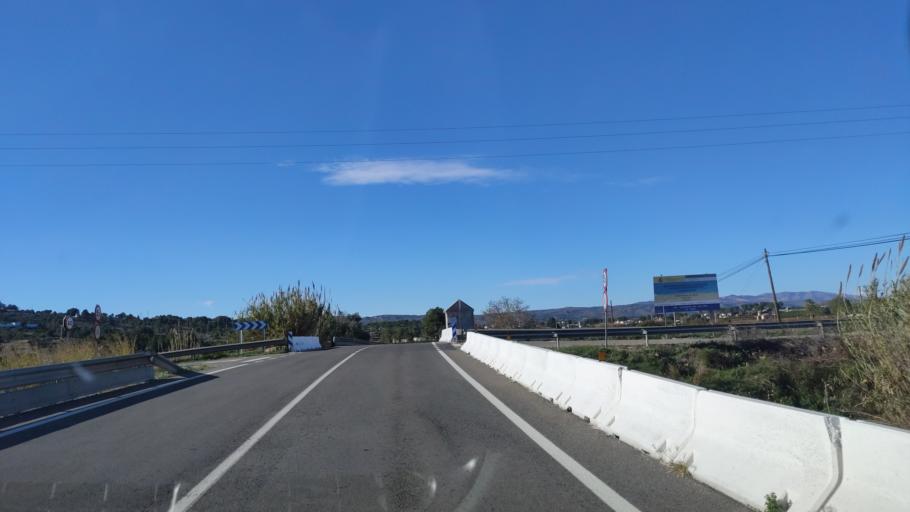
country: ES
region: Valencia
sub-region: Provincia de Valencia
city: Alberic
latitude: 39.1219
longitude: -0.5455
